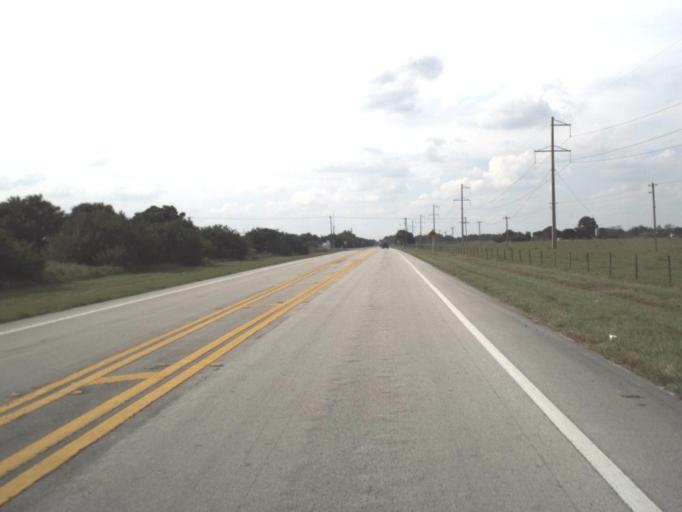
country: US
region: Florida
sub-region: Okeechobee County
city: Taylor Creek
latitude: 27.1917
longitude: -80.7267
